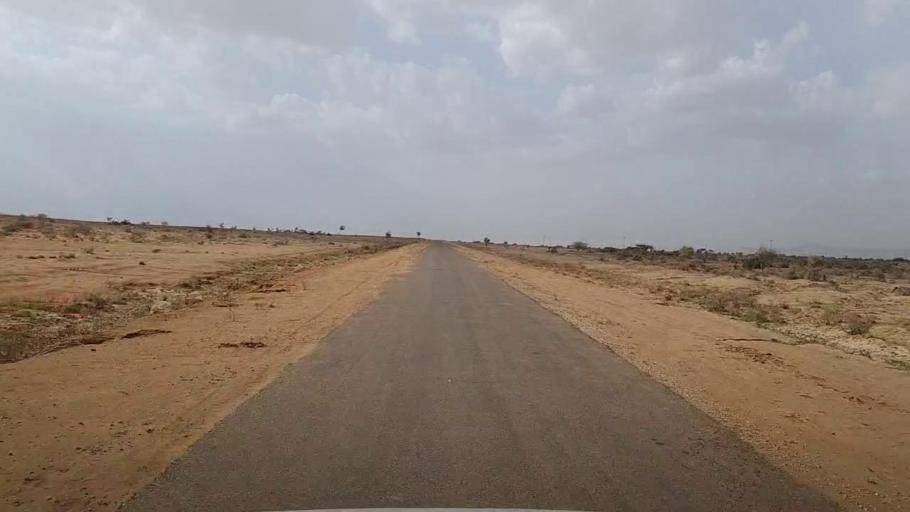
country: PK
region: Sindh
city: Jamshoro
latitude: 25.4639
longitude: 67.6773
